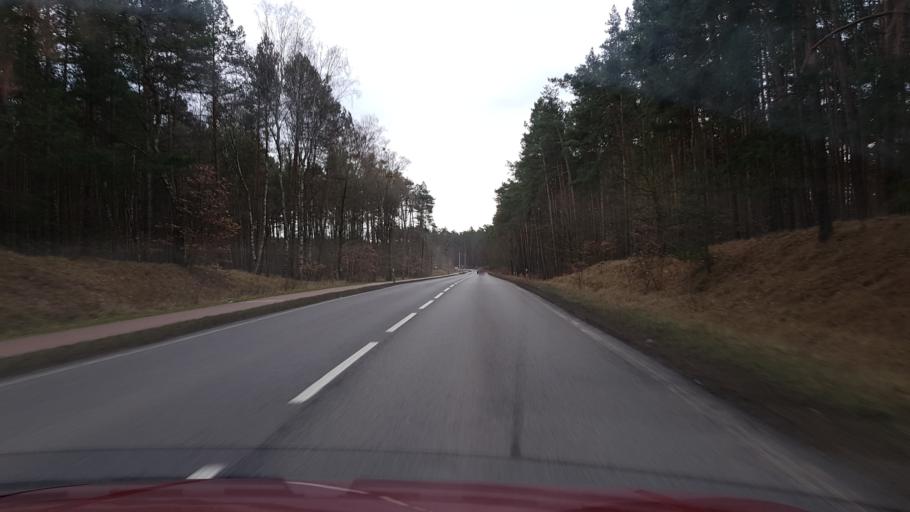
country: PL
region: West Pomeranian Voivodeship
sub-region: Powiat policki
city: Dobra
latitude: 53.5233
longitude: 14.4694
